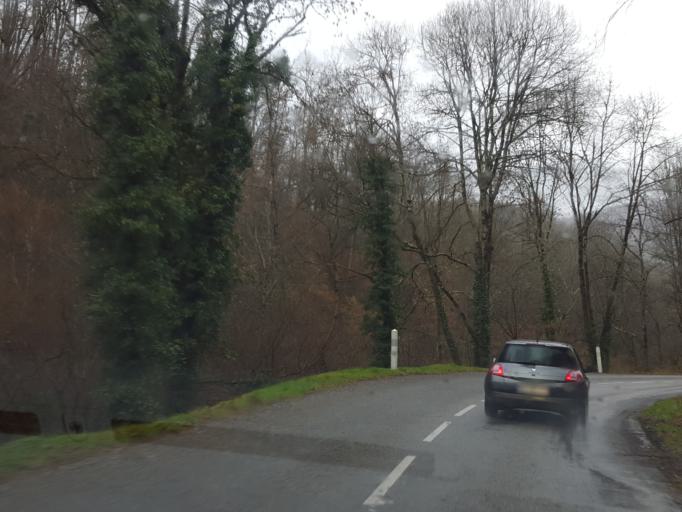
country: FR
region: Midi-Pyrenees
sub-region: Departement de l'Ariege
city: Saint-Girons
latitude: 42.9030
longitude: 1.2423
